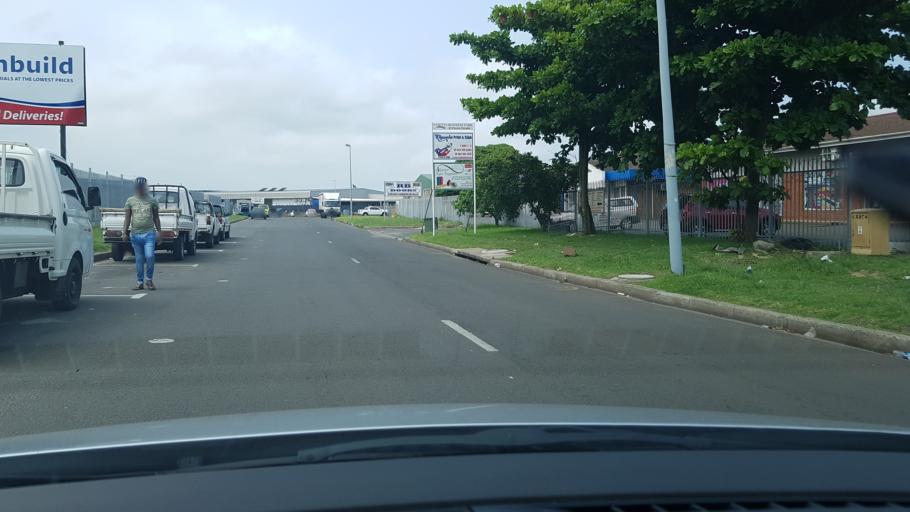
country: ZA
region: KwaZulu-Natal
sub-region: uThungulu District Municipality
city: Richards Bay
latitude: -28.7455
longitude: 32.0483
